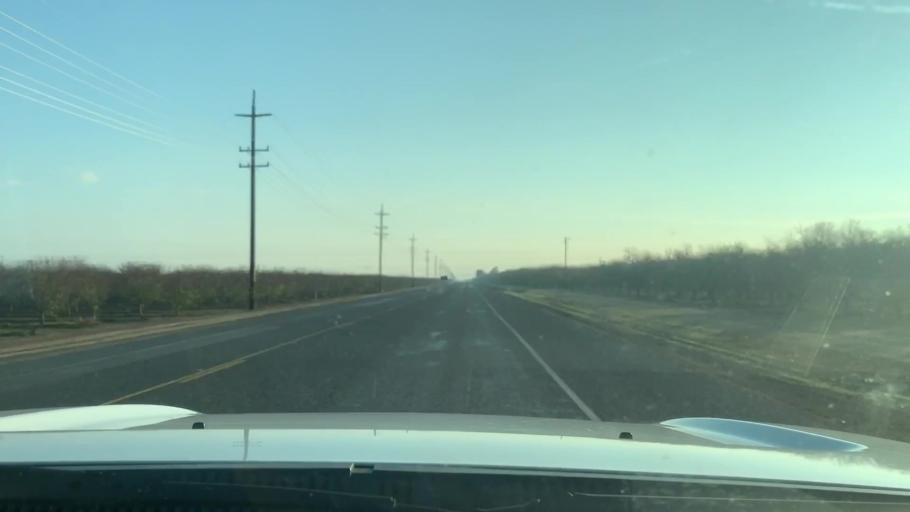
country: US
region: California
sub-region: Kern County
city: Wasco
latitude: 35.6014
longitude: -119.4352
